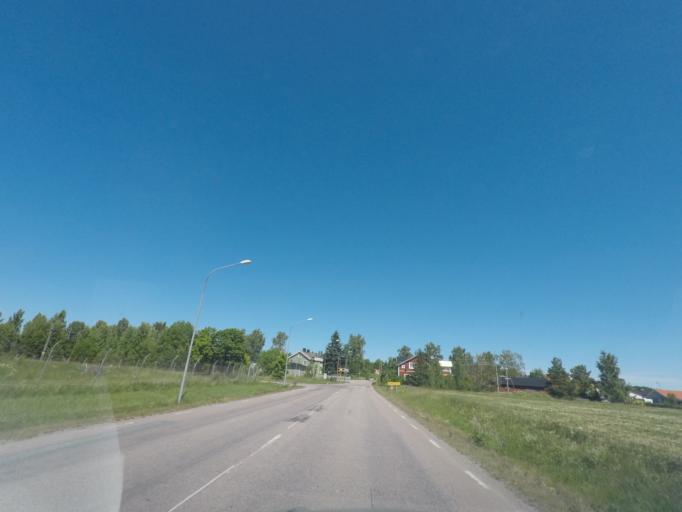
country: SE
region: Vaestmanland
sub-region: Vasteras
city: Tillberga
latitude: 59.6719
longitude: 16.7245
